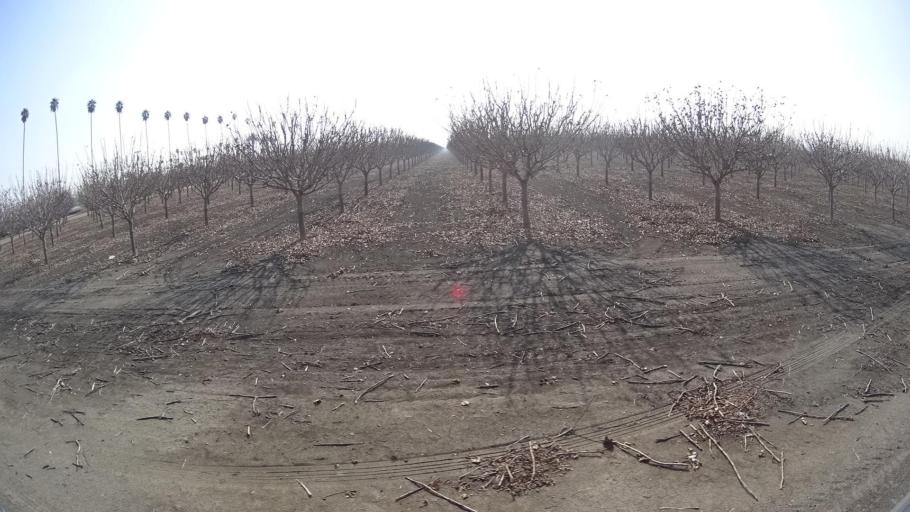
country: US
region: California
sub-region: Kern County
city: Buttonwillow
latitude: 35.3403
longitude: -119.3953
